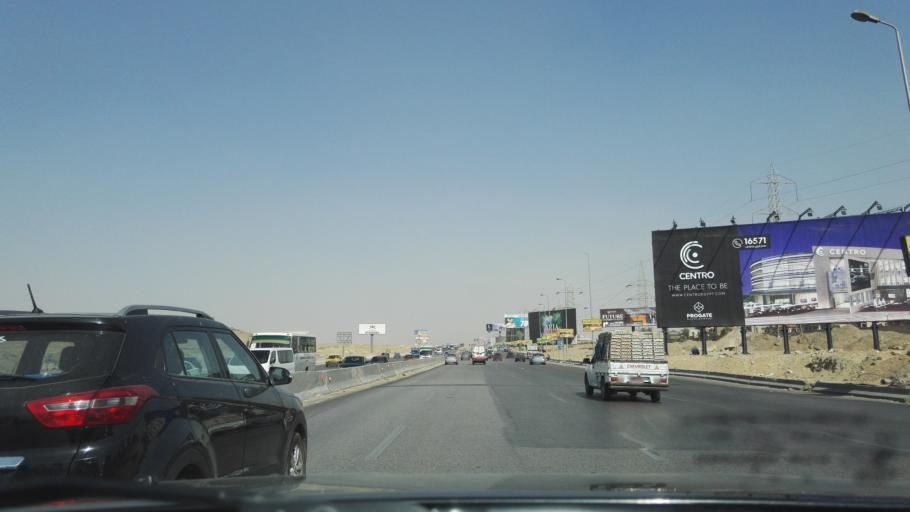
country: EG
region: Muhafazat al Qalyubiyah
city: Al Khankah
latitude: 30.0799
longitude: 31.4399
